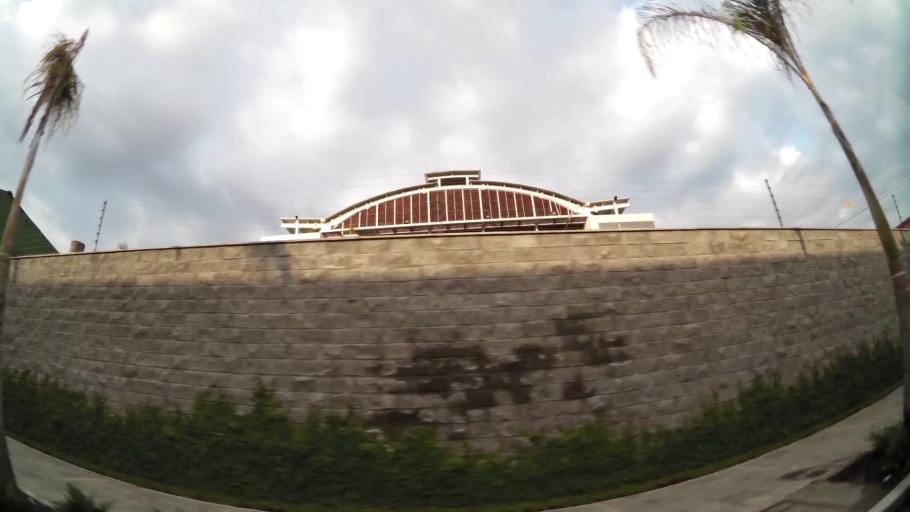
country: CO
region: Valle del Cauca
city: Cali
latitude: 3.4552
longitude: -76.5208
